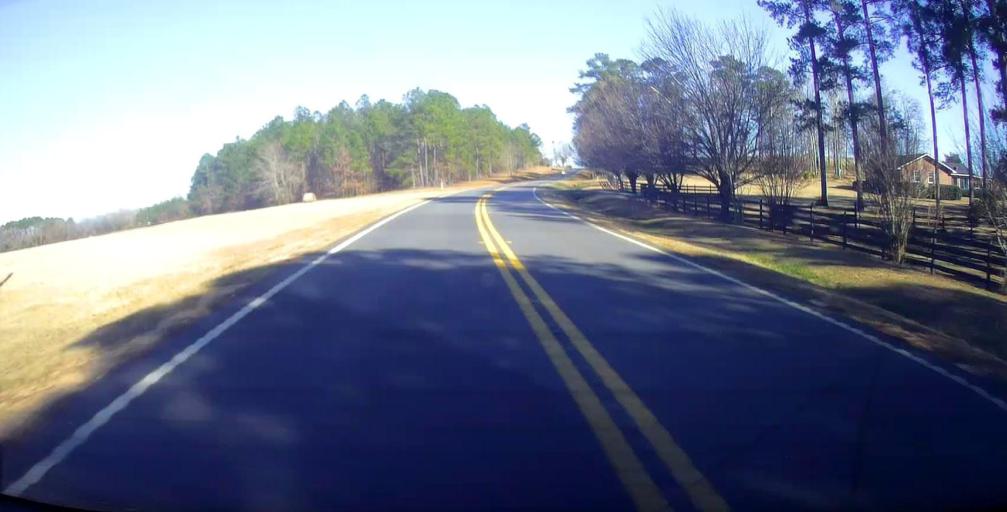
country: US
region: Georgia
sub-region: Taylor County
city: Butler
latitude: 32.6610
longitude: -84.3435
